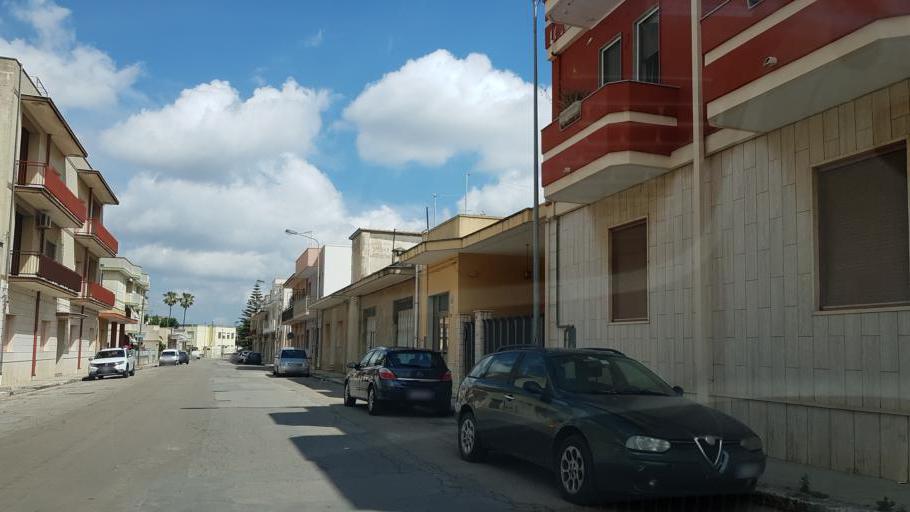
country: IT
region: Apulia
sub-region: Provincia di Brindisi
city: Mesagne
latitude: 40.5549
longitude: 17.8169
